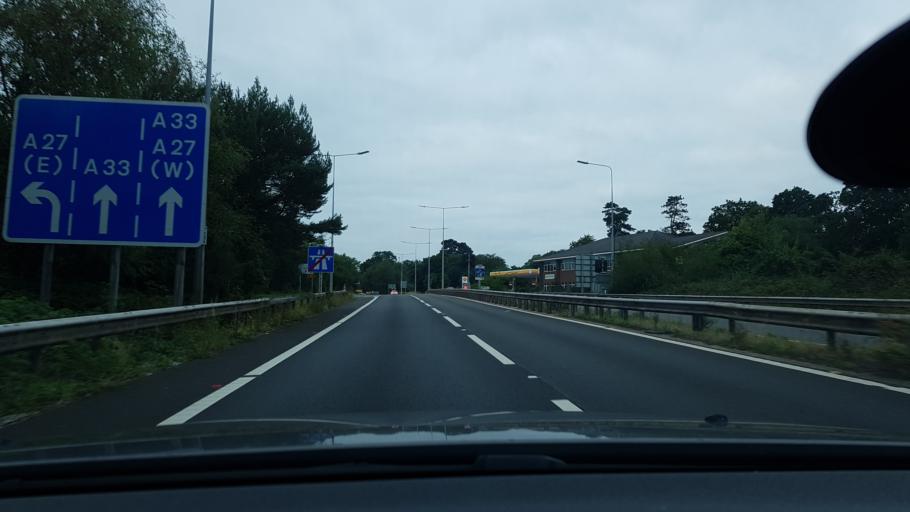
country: GB
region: England
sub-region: Southampton
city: Southampton
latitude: 50.9545
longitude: -1.4028
